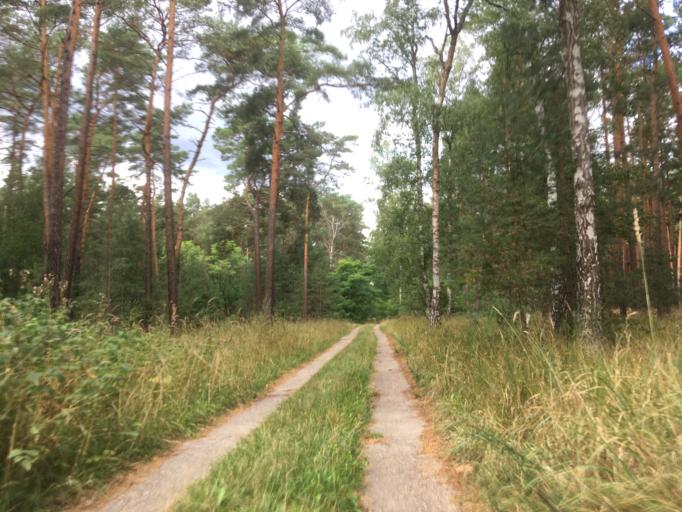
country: DE
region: Brandenburg
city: Wildau
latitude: 52.3293
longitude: 13.6975
